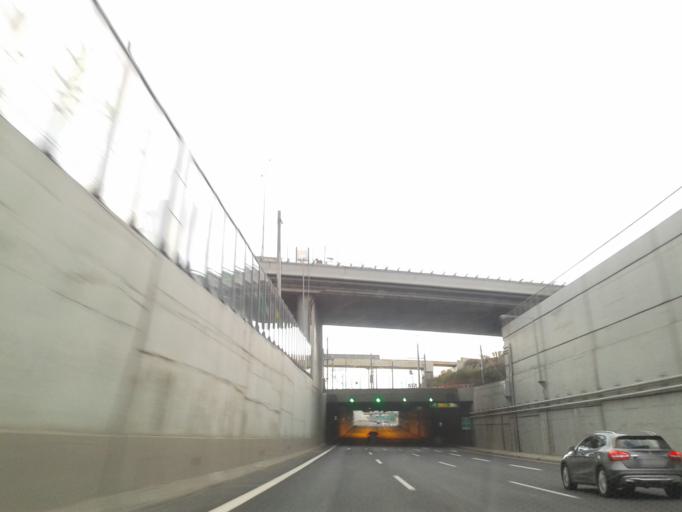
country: GR
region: Attica
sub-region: Nomarchia Anatolikis Attikis
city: Acharnes
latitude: 38.0655
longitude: 23.7380
